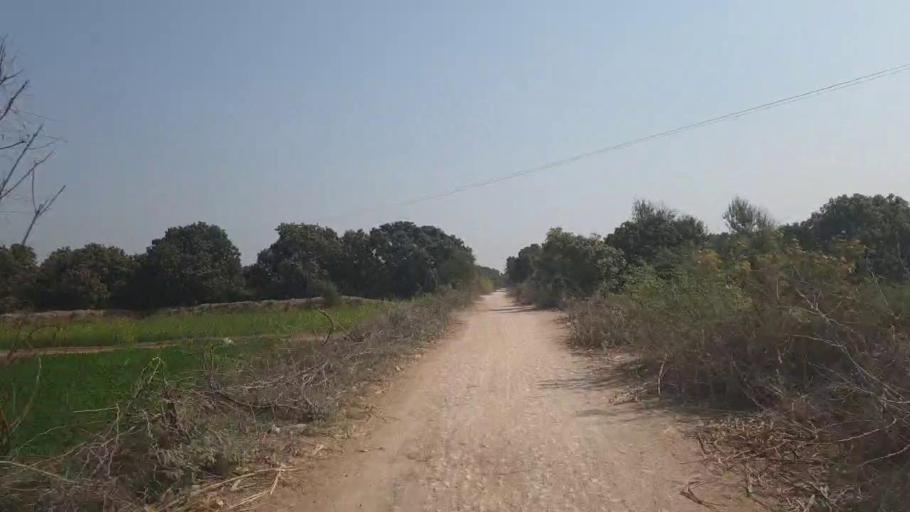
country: PK
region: Sindh
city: Tando Allahyar
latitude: 25.4336
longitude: 68.8451
